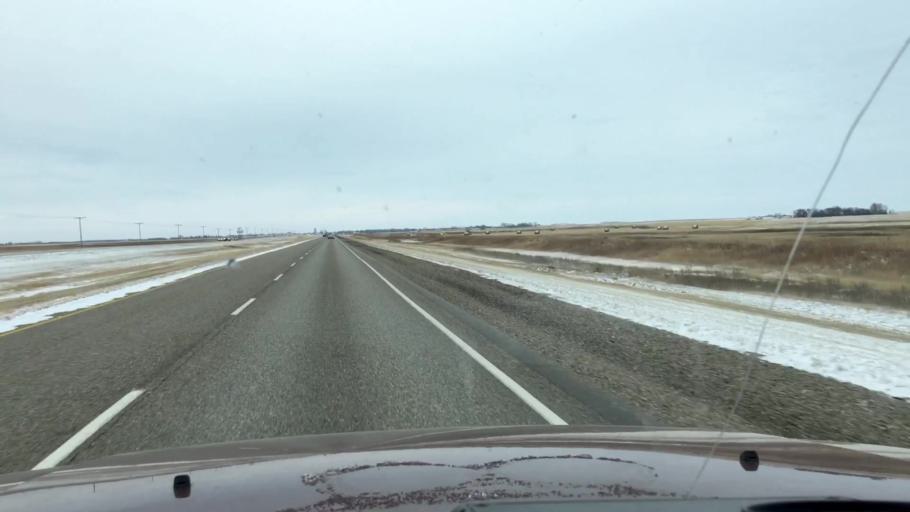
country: CA
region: Saskatchewan
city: Watrous
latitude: 51.0836
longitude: -105.8515
